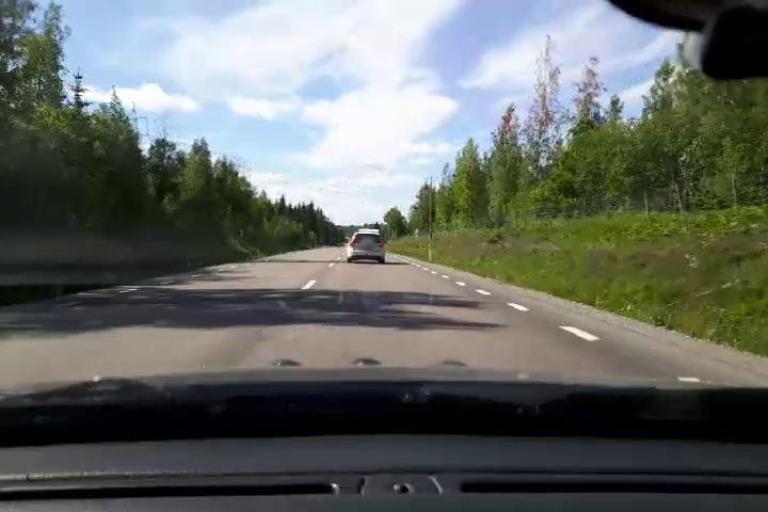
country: SE
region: Gaevleborg
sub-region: Bollnas Kommun
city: Kilafors
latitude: 61.2892
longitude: 16.5075
